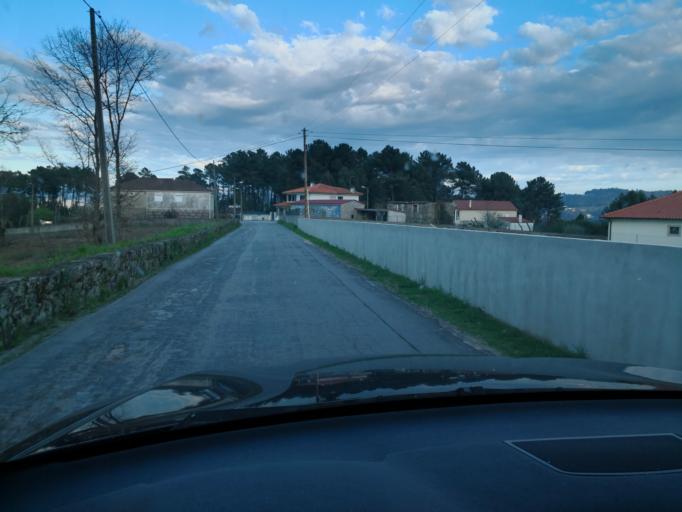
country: PT
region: Vila Real
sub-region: Vila Real
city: Vila Real
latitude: 41.3006
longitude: -7.7770
